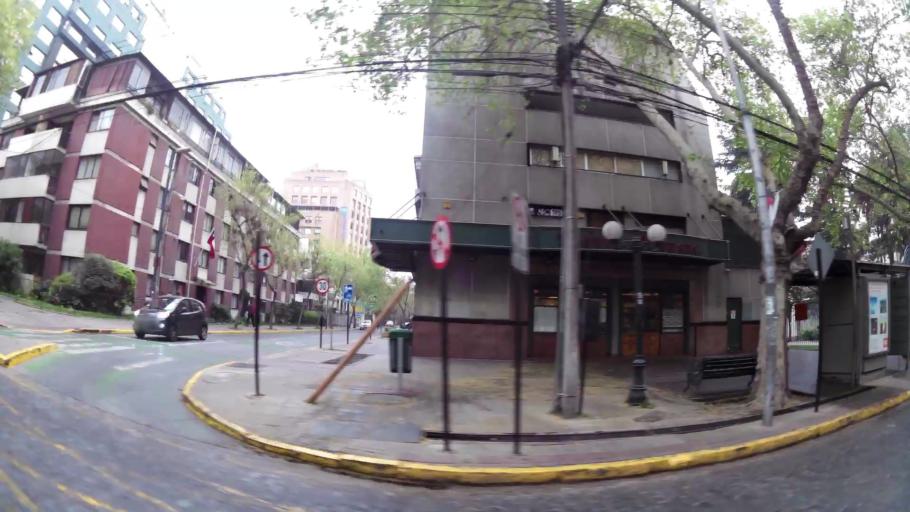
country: CL
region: Santiago Metropolitan
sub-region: Provincia de Santiago
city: Villa Presidente Frei, Nunoa, Santiago, Chile
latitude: -33.4253
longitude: -70.6117
